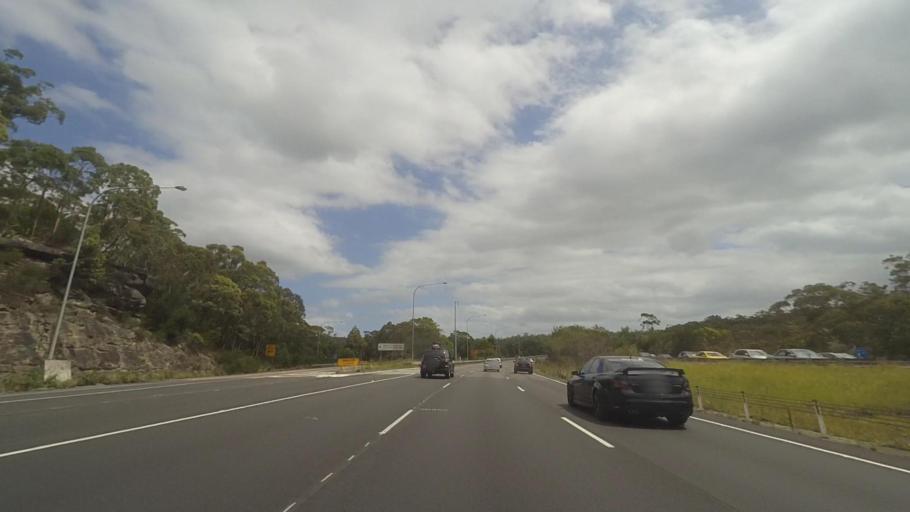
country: AU
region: New South Wales
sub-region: Gosford Shire
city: Point Clare
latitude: -33.4470
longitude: 151.2187
